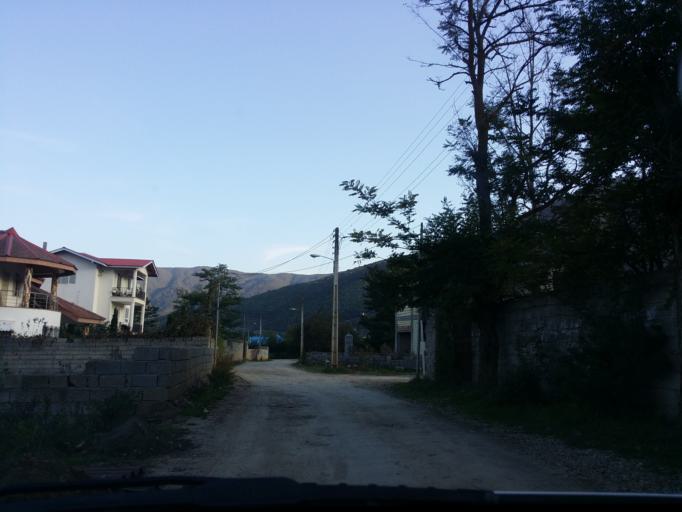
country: IR
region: Mazandaran
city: `Abbasabad
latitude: 36.5110
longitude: 51.1839
